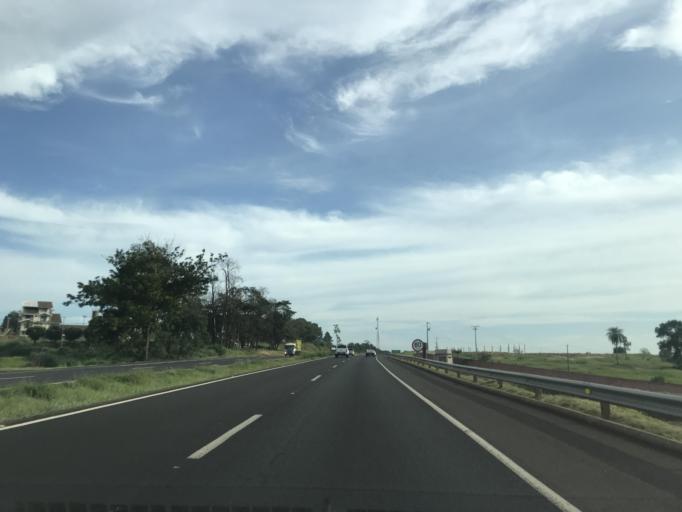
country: BR
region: Parana
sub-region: Mandaguacu
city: Mandaguacu
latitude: -23.3274
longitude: -52.1114
